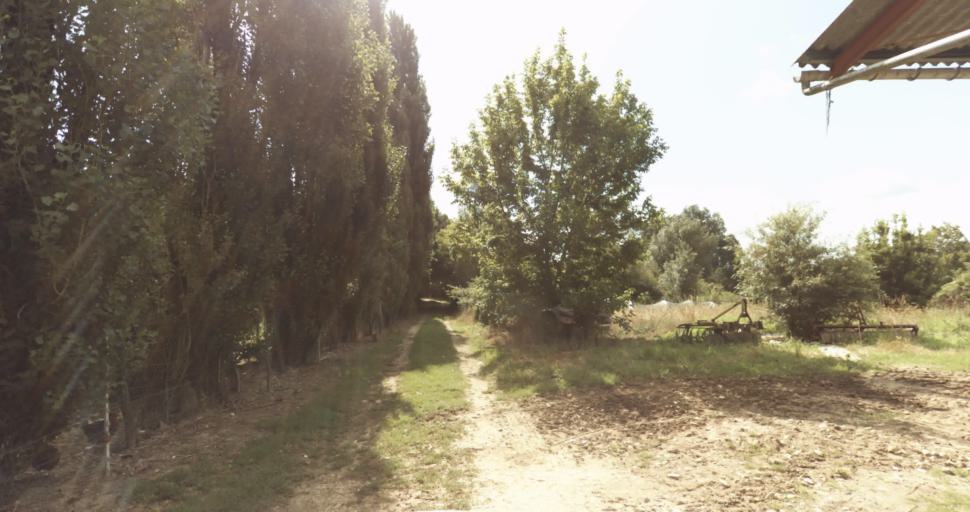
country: FR
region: Aquitaine
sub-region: Departement de la Gironde
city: Bazas
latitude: 44.4372
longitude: -0.1921
